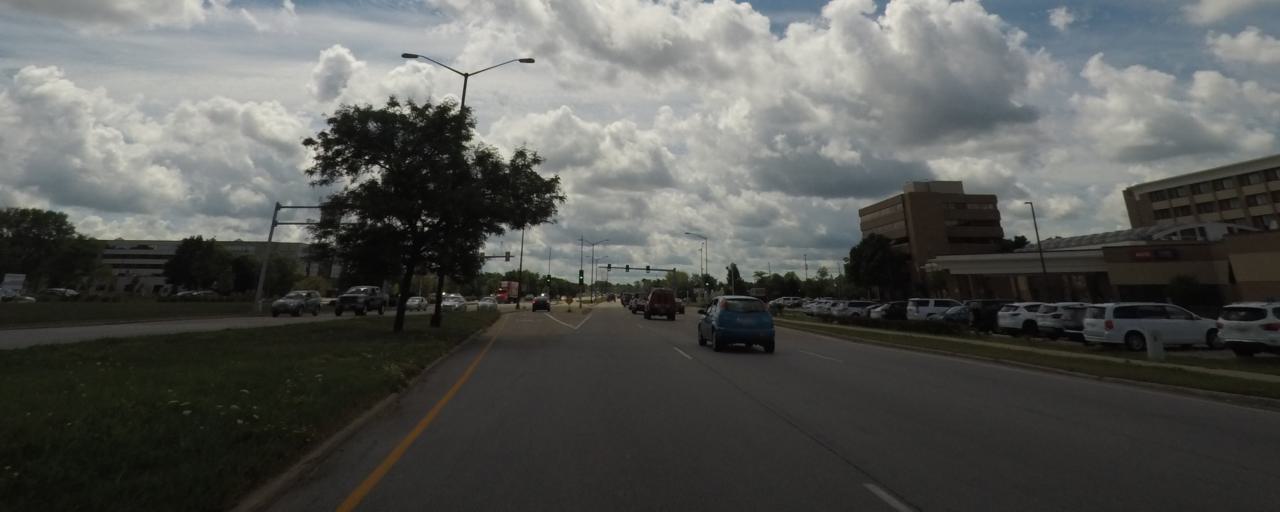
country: US
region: Wisconsin
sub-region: Waukesha County
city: Elm Grove
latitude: 43.0224
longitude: -88.1072
